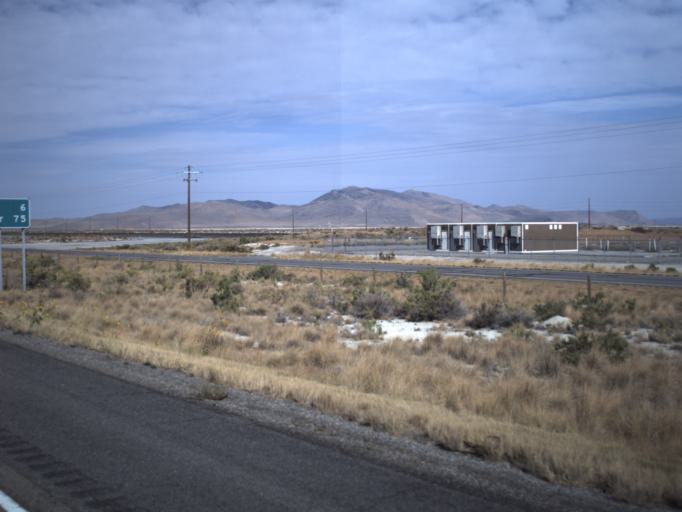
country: US
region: Utah
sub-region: Tooele County
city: Grantsville
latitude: 40.7479
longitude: -112.6701
